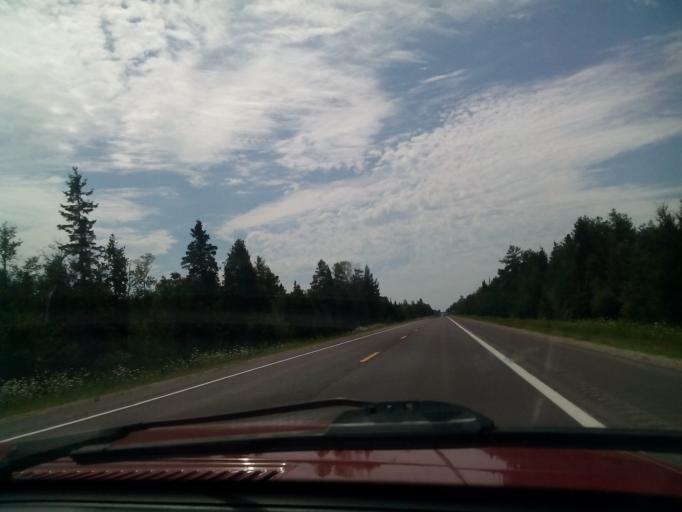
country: US
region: Michigan
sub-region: Schoolcraft County
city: Manistique
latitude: 46.0340
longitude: -85.9780
